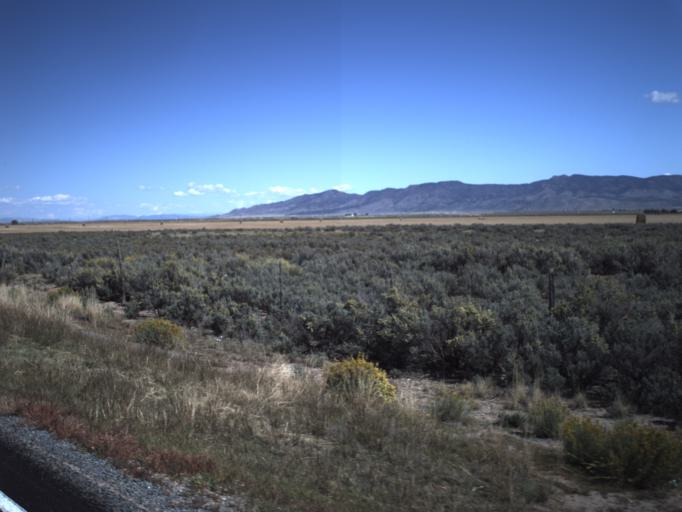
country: US
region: Utah
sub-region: Washington County
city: Enterprise
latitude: 37.6723
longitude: -113.6601
